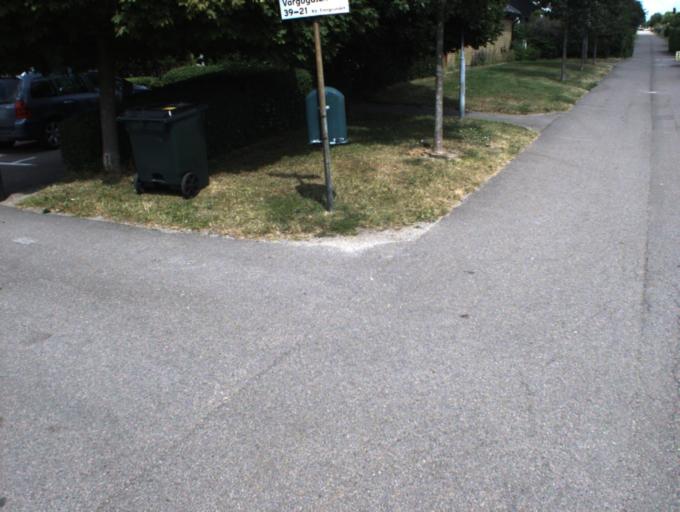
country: SE
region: Skane
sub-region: Helsingborg
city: Rydeback
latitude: 55.9706
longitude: 12.7649
